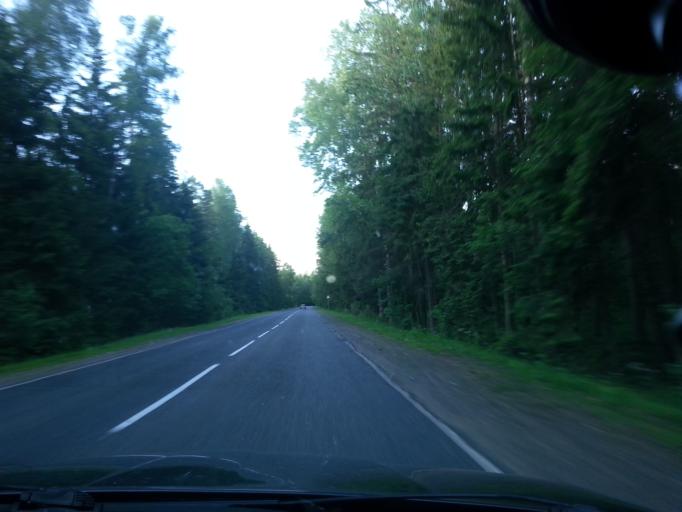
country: BY
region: Minsk
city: Svir
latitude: 54.9259
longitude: 26.5396
